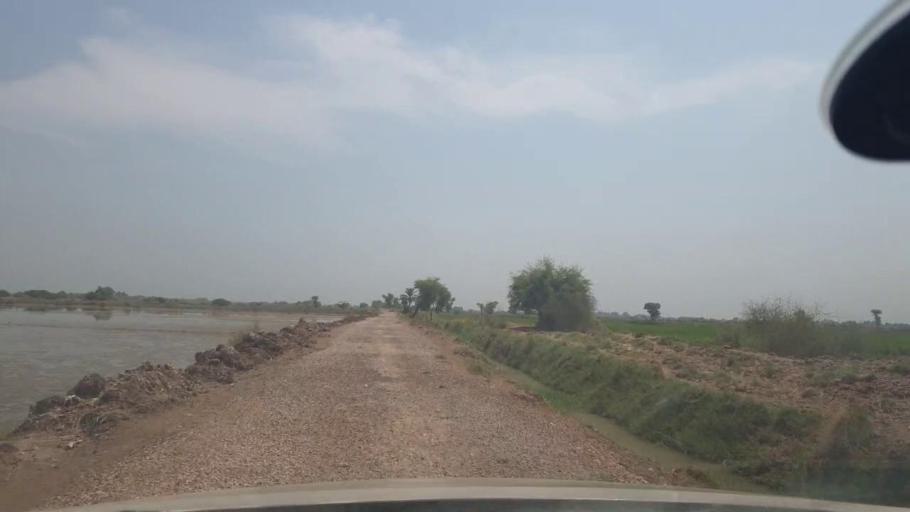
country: PK
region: Sindh
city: Jacobabad
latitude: 28.2285
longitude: 68.3952
